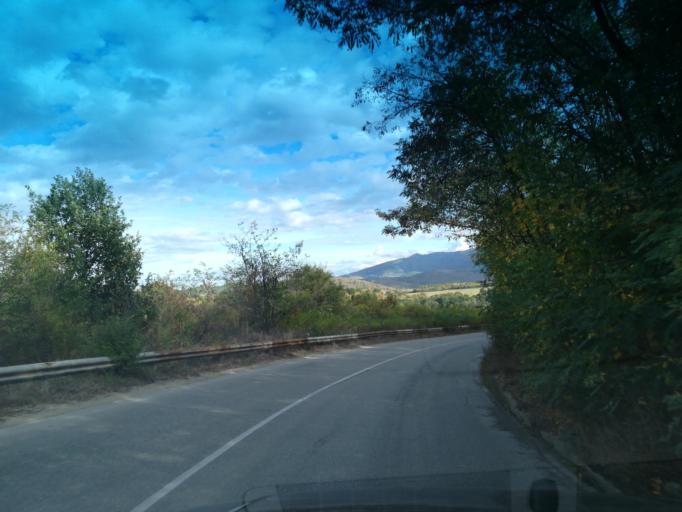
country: BG
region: Pazardzhik
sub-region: Obshtina Peshtera
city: Peshtera
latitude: 42.0489
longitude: 24.3253
